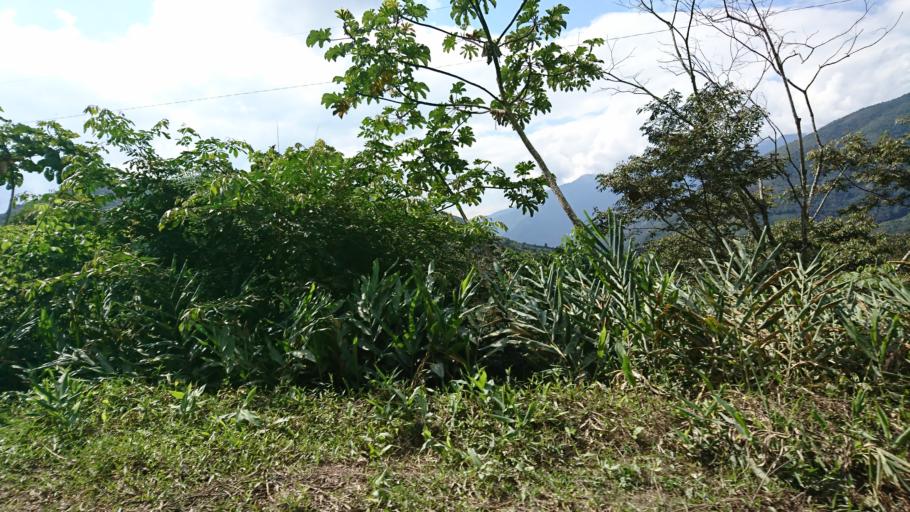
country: BO
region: La Paz
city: Coroico
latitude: -16.1190
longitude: -67.7654
